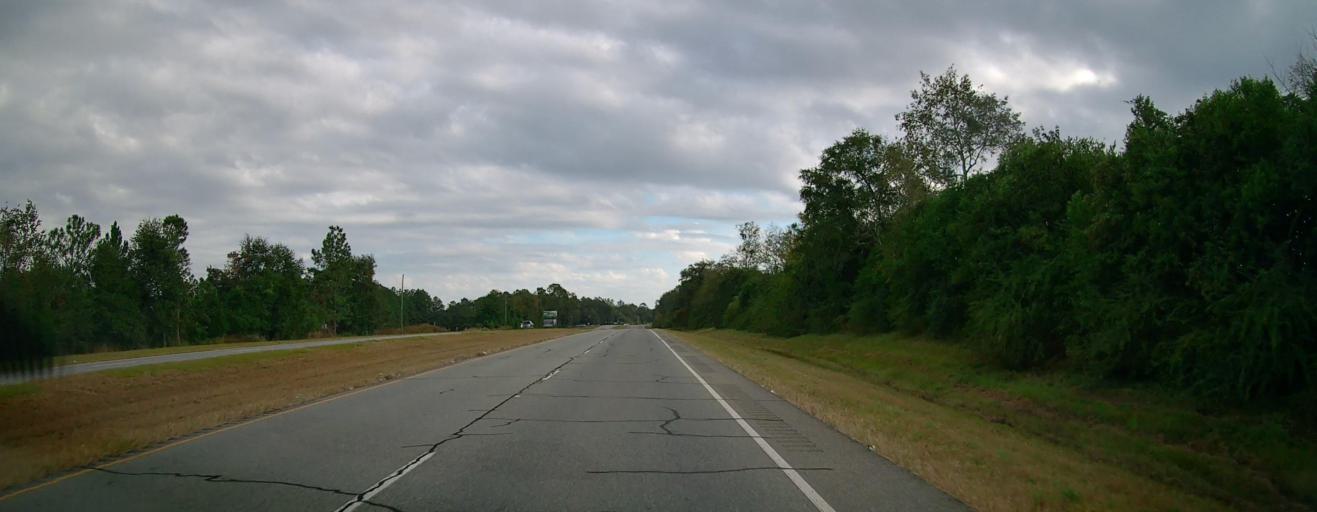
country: US
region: Georgia
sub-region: Thomas County
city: Meigs
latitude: 31.0829
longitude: -84.0850
